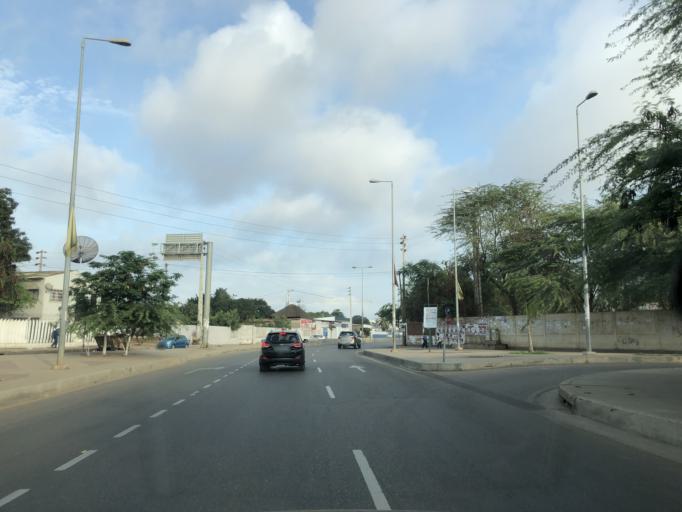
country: AO
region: Luanda
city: Luanda
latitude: -8.8920
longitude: 13.2105
